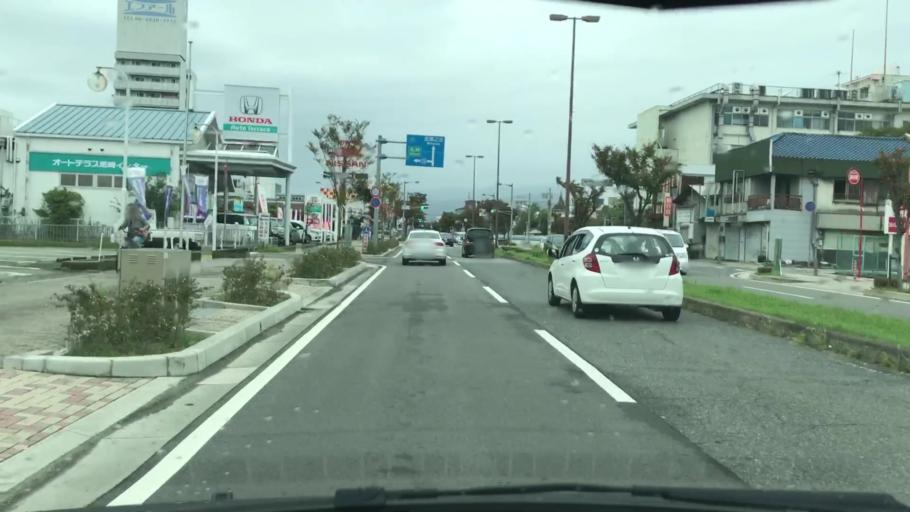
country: JP
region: Hyogo
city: Amagasaki
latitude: 34.7436
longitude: 135.4166
